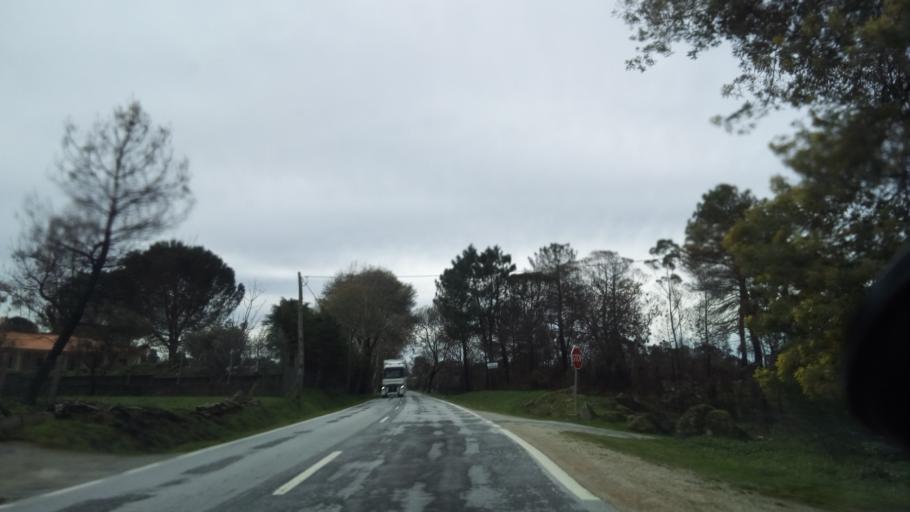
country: PT
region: Guarda
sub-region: Seia
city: Seia
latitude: 40.5181
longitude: -7.6233
